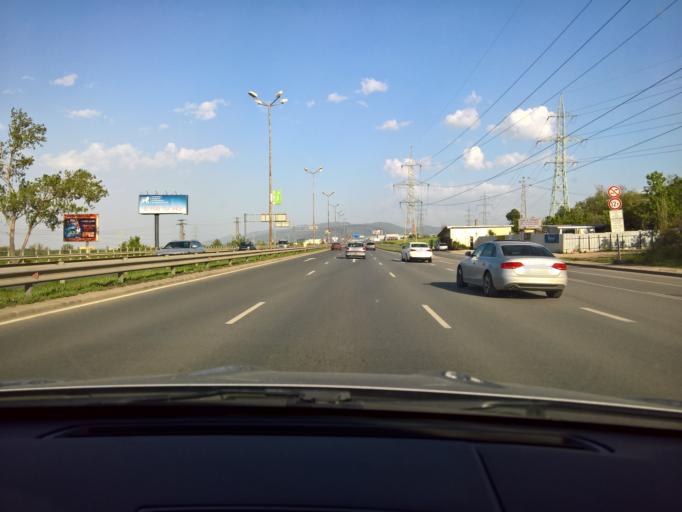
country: BG
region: Sofia-Capital
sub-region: Stolichna Obshtina
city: Sofia
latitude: 42.6298
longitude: 23.3413
